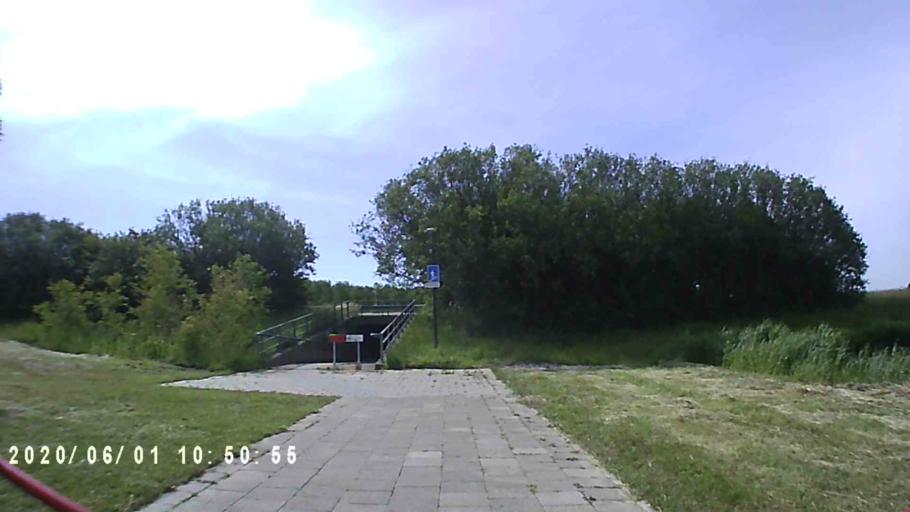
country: NL
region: Friesland
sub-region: Gemeente Franekeradeel
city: Franeker
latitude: 53.1986
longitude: 5.5207
